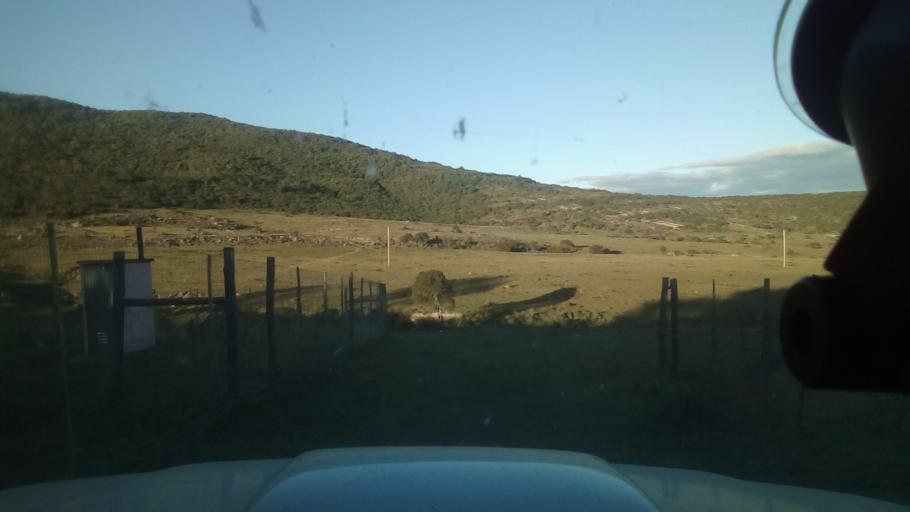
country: ZA
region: Eastern Cape
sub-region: Buffalo City Metropolitan Municipality
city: Bhisho
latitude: -32.7358
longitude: 27.3791
